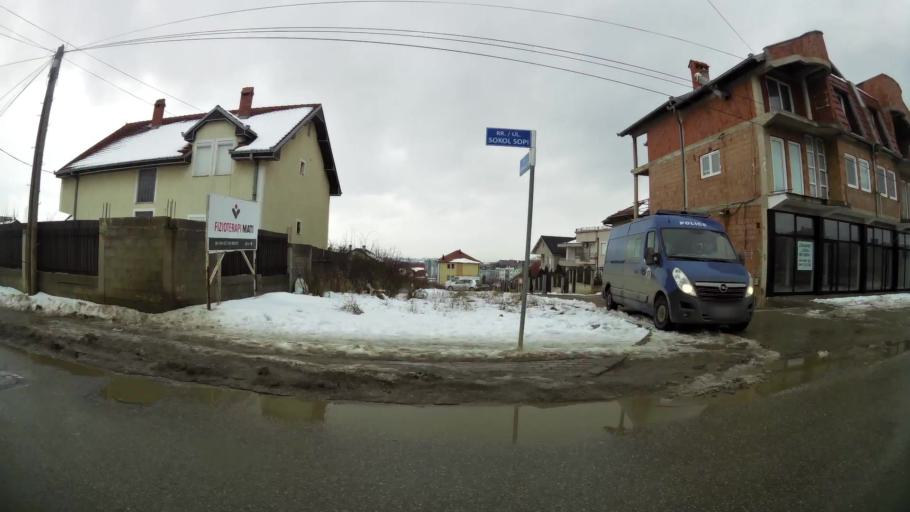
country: XK
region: Pristina
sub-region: Komuna e Prishtines
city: Pristina
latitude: 42.6556
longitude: 21.1890
